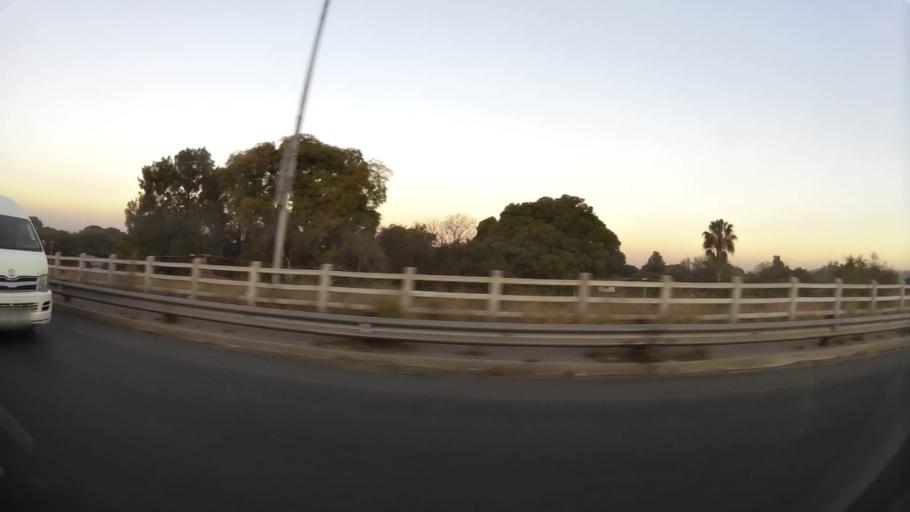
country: ZA
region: North-West
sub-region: Bojanala Platinum District Municipality
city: Rustenburg
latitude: -25.6555
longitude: 27.2446
